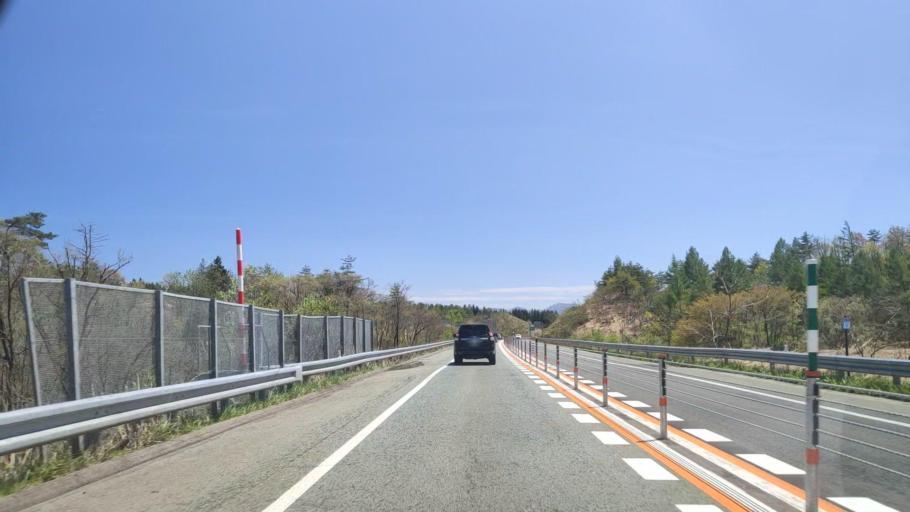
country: JP
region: Yamagata
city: Obanazawa
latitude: 38.6509
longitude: 140.3704
